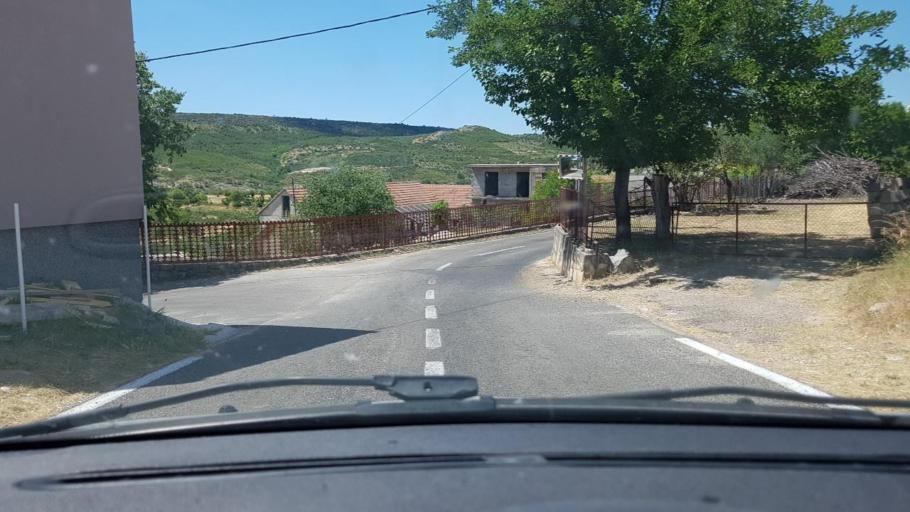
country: HR
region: Sibensko-Kniniska
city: Kistanje
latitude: 43.9075
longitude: 15.9207
